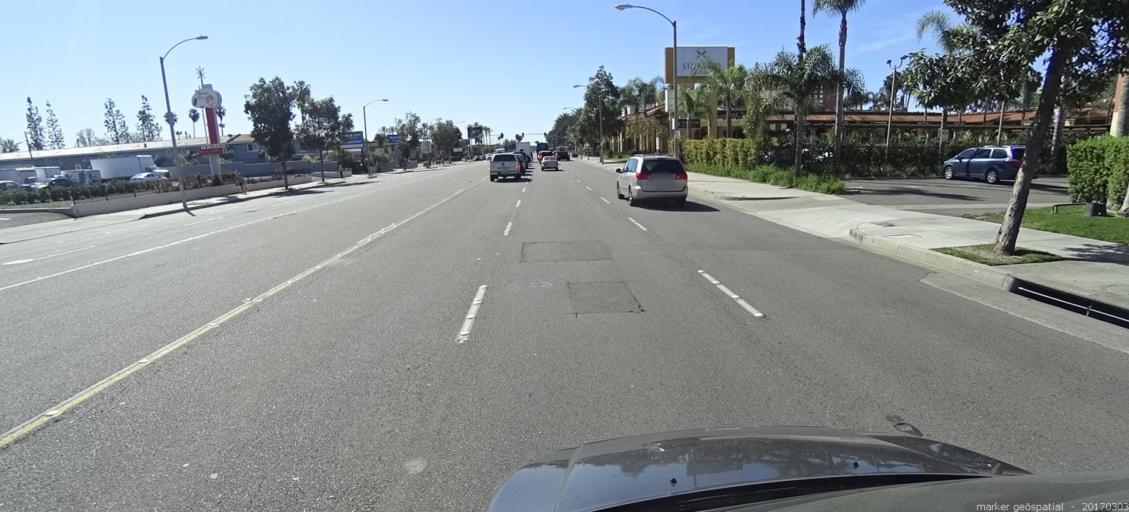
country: US
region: California
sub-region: Orange County
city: Garden Grove
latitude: 33.7944
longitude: -117.9152
